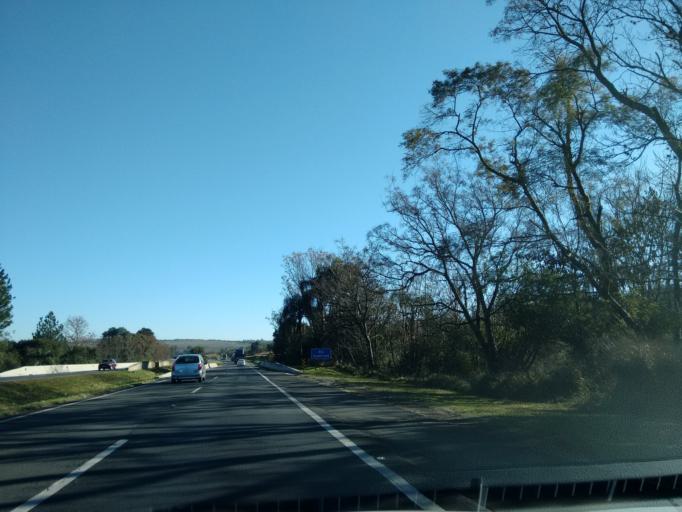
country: BR
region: Parana
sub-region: Palmeira
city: Palmeira
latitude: -25.2521
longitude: -50.0172
